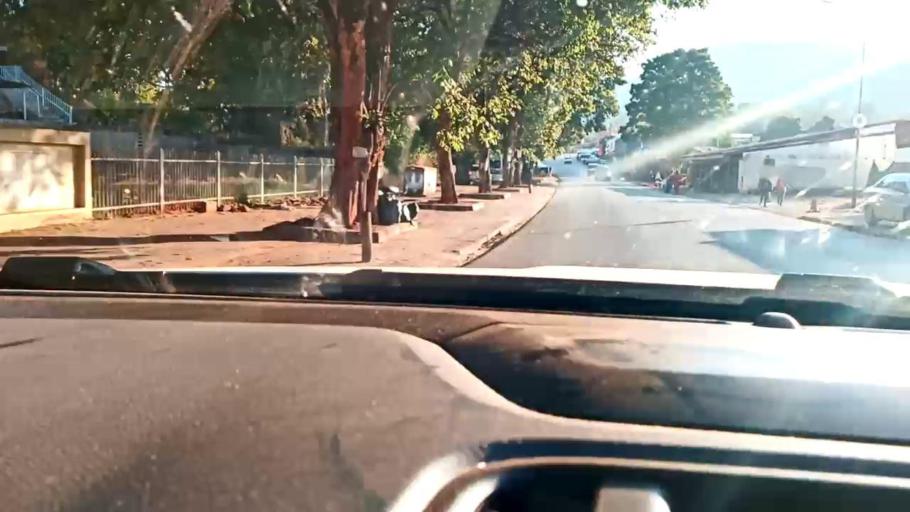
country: ZA
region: Limpopo
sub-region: Mopani District Municipality
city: Duiwelskloof
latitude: -23.6951
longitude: 30.1435
